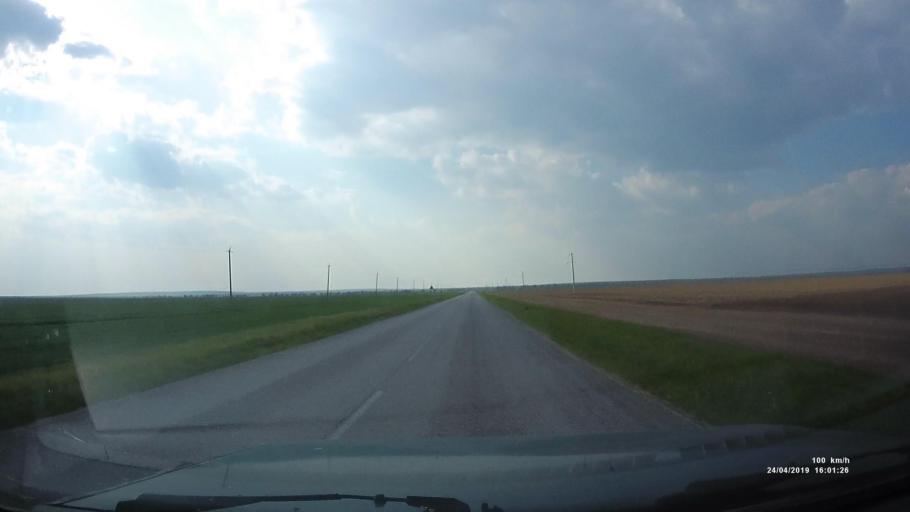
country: RU
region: Rostov
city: Sovetskoye
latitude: 46.6417
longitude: 42.4361
